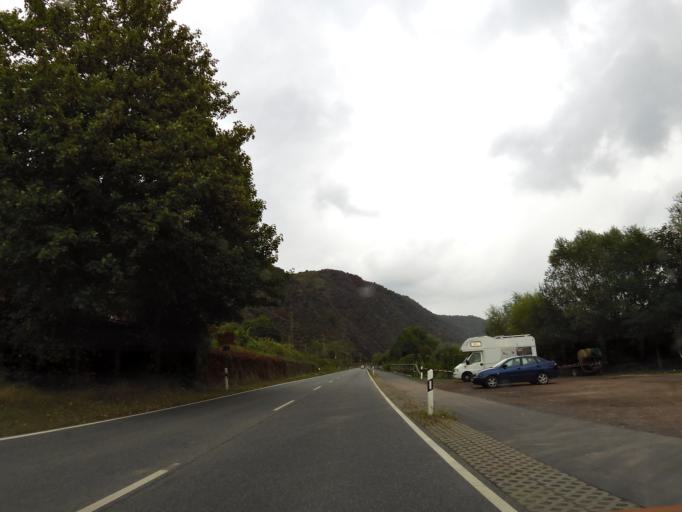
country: DE
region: Rheinland-Pfalz
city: Klotten
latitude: 50.1660
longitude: 7.2051
